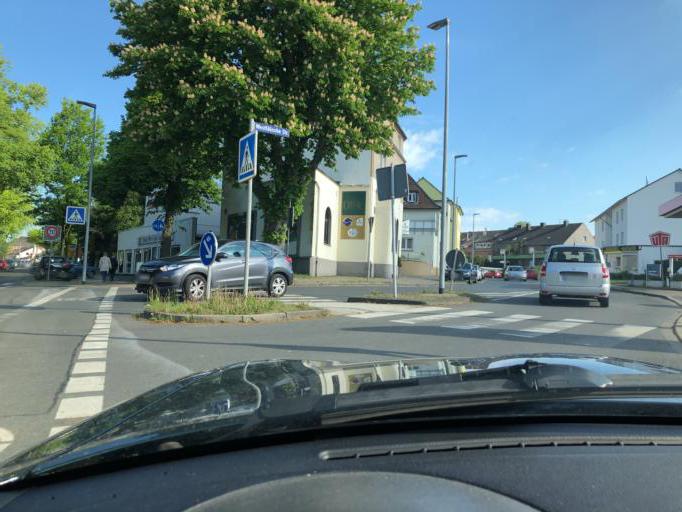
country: DE
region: North Rhine-Westphalia
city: Bochum-Hordel
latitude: 51.4618
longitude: 7.1545
